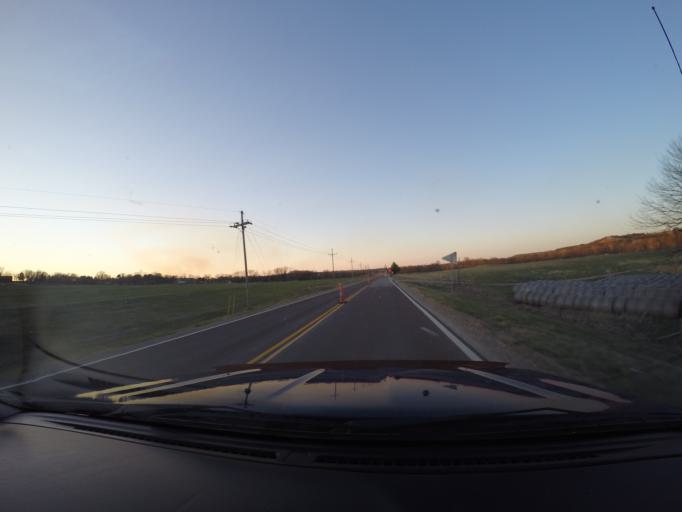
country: US
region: Kansas
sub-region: Wabaunsee County
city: Alma
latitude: 38.9969
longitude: -96.2836
